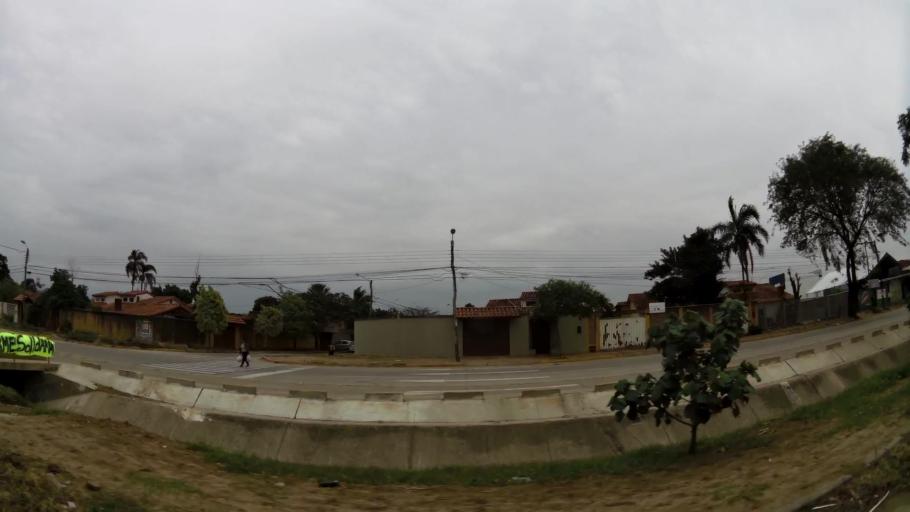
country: BO
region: Santa Cruz
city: Santa Cruz de la Sierra
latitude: -17.8372
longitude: -63.1740
